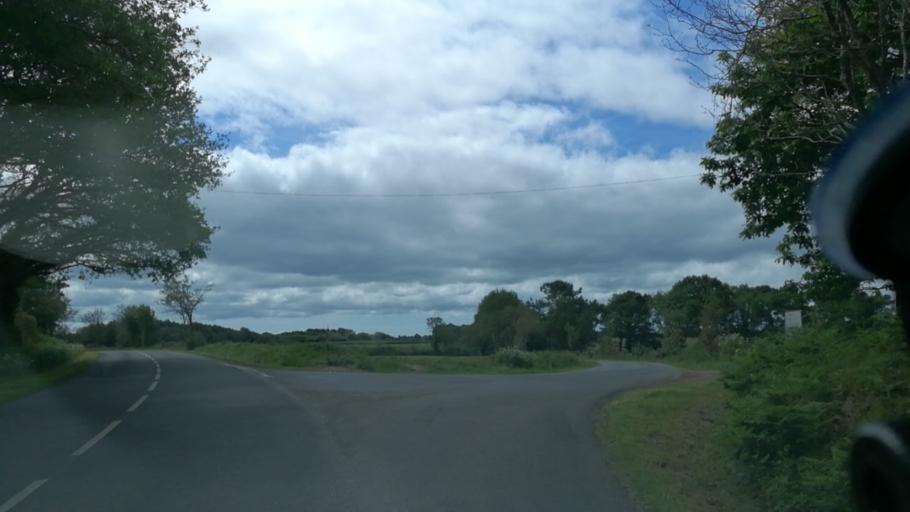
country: FR
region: Pays de la Loire
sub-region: Departement de la Loire-Atlantique
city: Asserac
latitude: 47.4478
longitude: -2.4121
